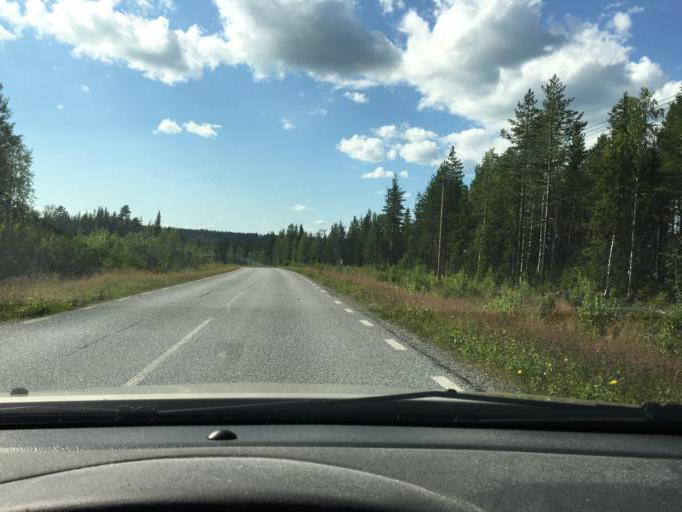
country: SE
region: Norrbotten
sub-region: Kalix Kommun
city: Toere
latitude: 66.0537
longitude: 22.5661
